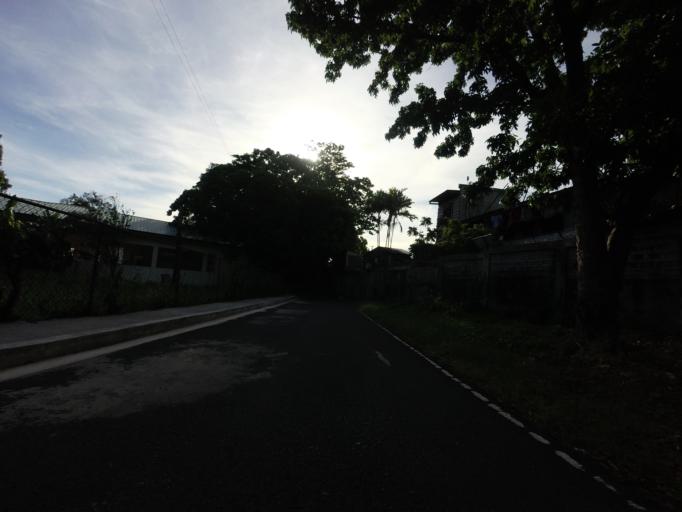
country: PH
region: Metro Manila
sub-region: Mandaluyong
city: Mandaluyong City
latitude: 14.5849
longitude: 121.0426
